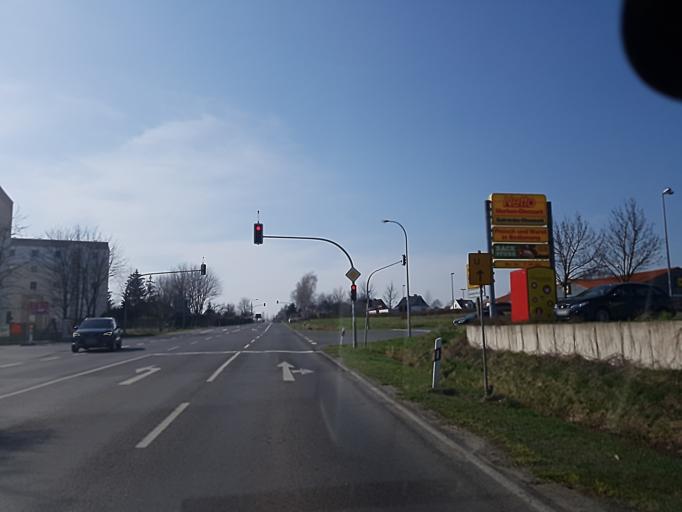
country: DE
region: Brandenburg
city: Calau
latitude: 51.7483
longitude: 13.9548
